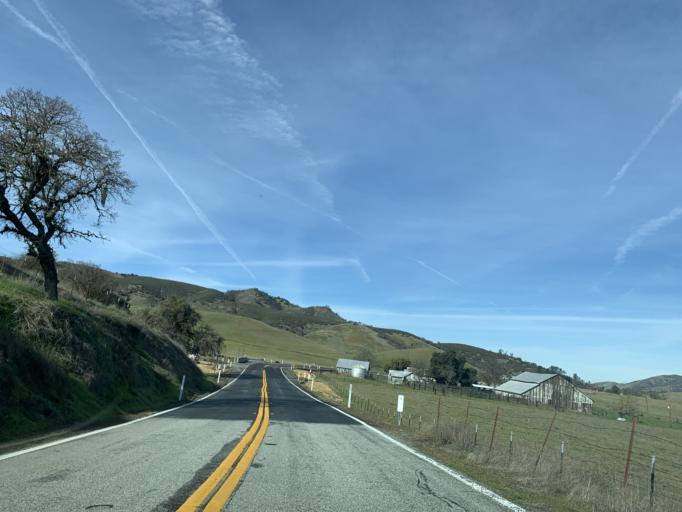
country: US
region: California
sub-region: Monterey County
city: Soledad
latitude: 36.5657
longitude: -121.1819
